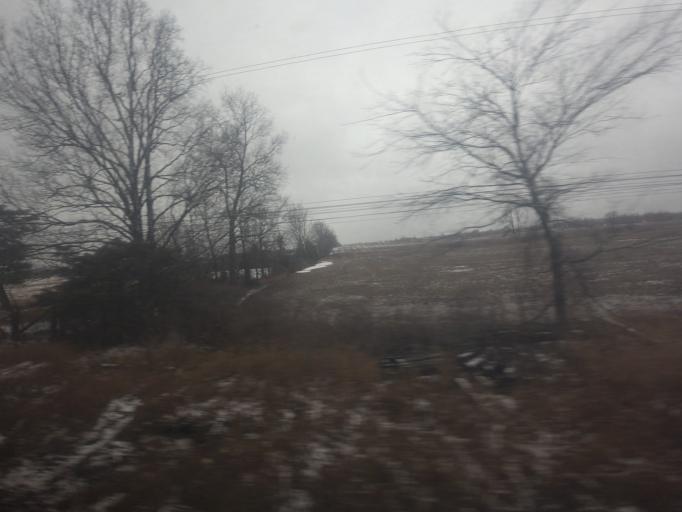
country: CA
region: Ontario
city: Deseronto
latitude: 44.2263
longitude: -77.0599
